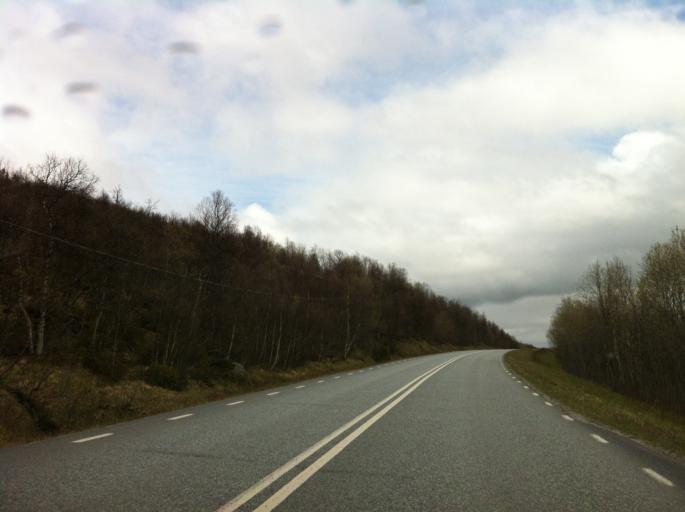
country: NO
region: Sor-Trondelag
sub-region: Tydal
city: Aas
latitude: 62.5693
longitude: 12.2429
